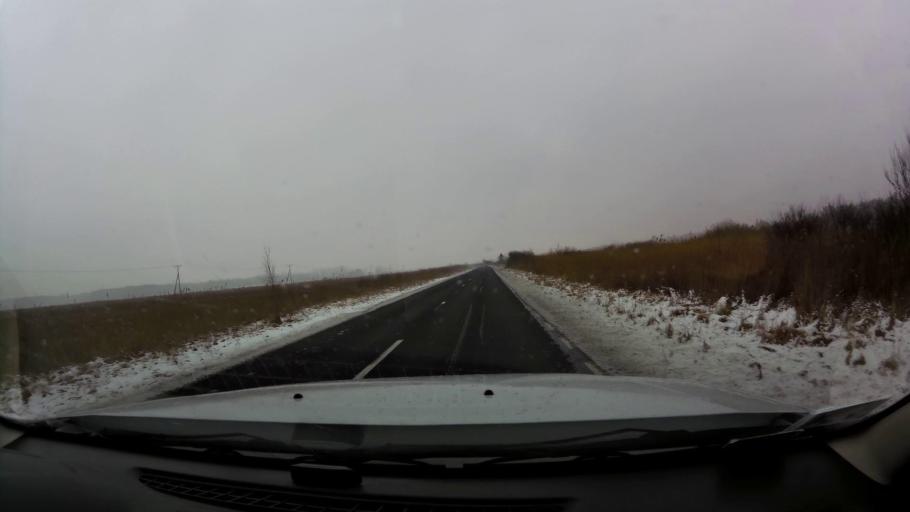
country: PL
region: West Pomeranian Voivodeship
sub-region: Powiat gryficki
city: Mrzezyno
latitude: 54.1171
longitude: 15.2674
